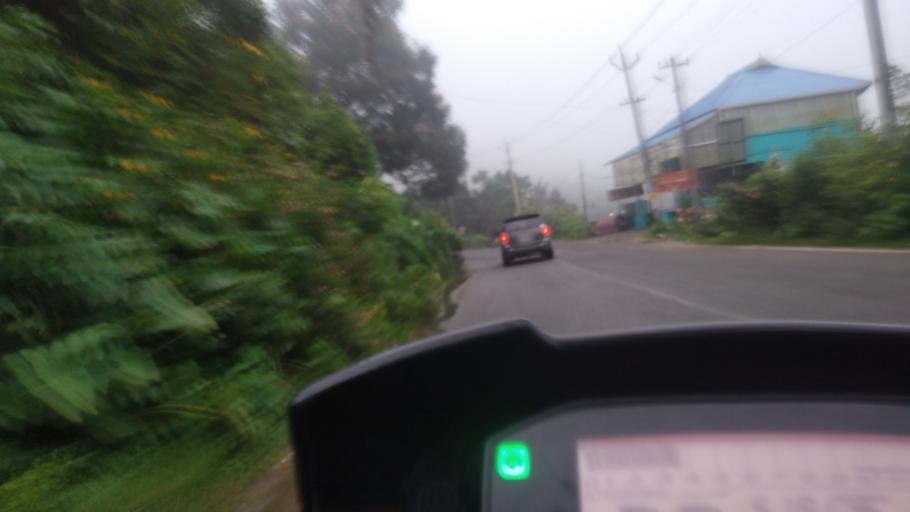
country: IN
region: Kerala
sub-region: Kottayam
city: Erattupetta
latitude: 9.5744
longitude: 76.9917
